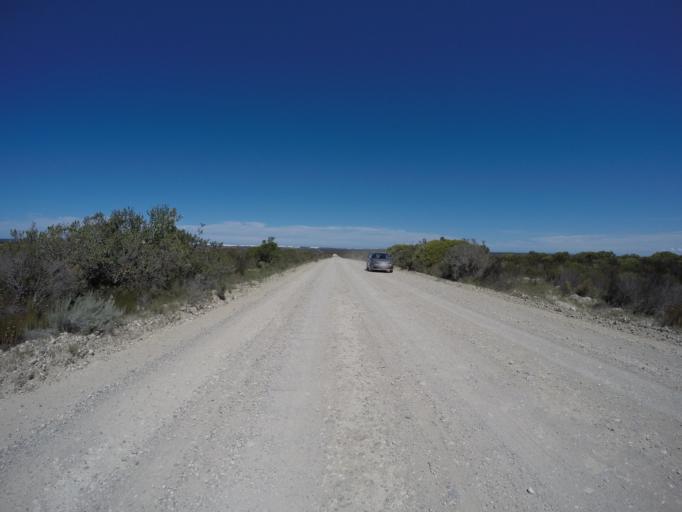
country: ZA
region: Western Cape
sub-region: Overberg District Municipality
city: Bredasdorp
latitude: -34.4387
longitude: 20.4207
